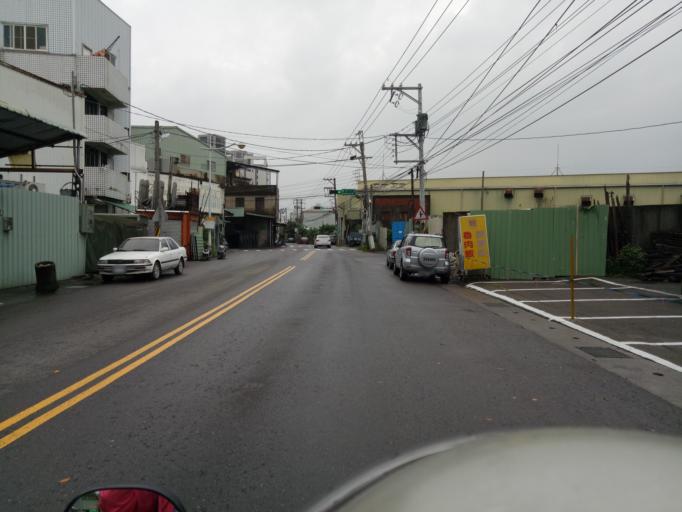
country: TW
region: Taiwan
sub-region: Taichung City
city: Taichung
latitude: 24.1110
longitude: 120.7103
